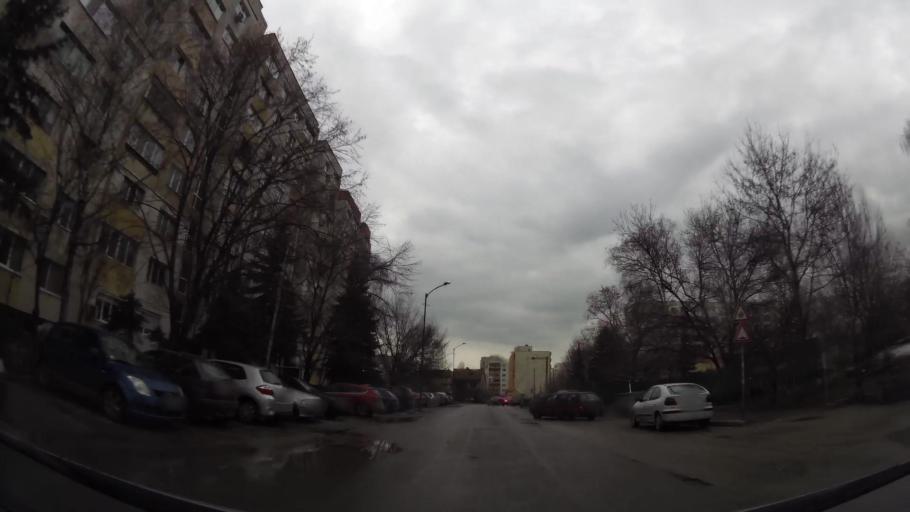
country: BG
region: Sofia-Capital
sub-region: Stolichna Obshtina
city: Sofia
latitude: 42.7305
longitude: 23.2930
